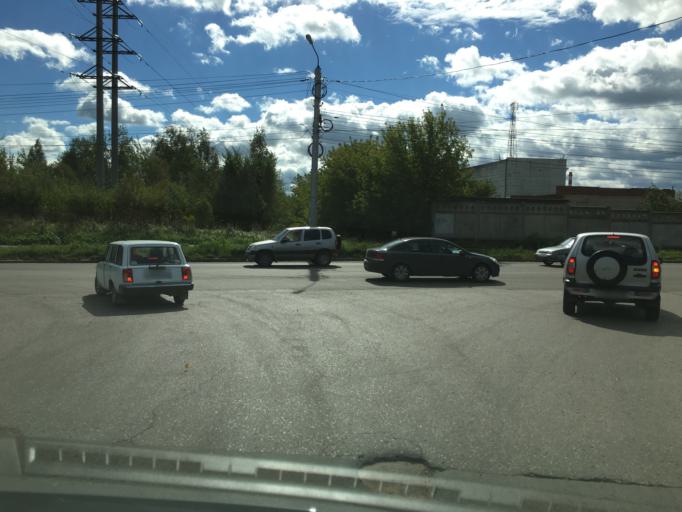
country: RU
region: Kaluga
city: Kaluga
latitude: 54.5411
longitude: 36.3168
